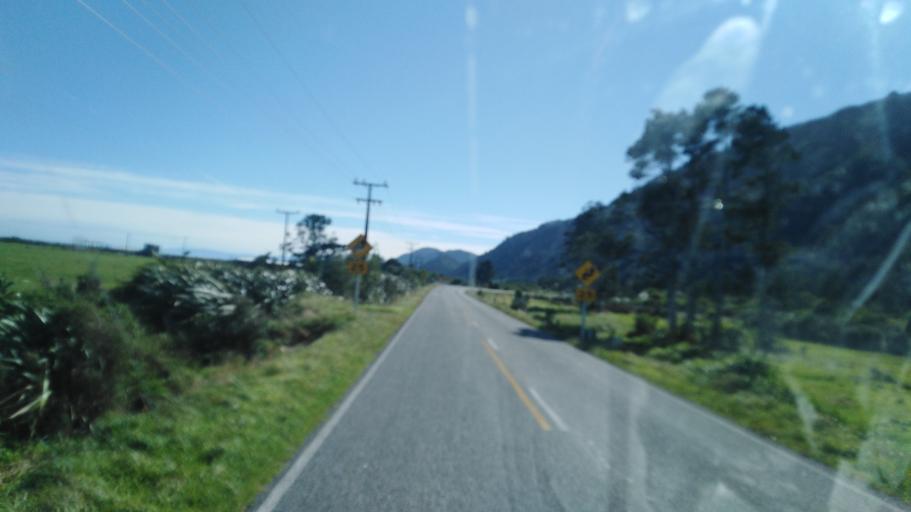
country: NZ
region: West Coast
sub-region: Buller District
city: Westport
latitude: -41.6522
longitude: 171.8280
